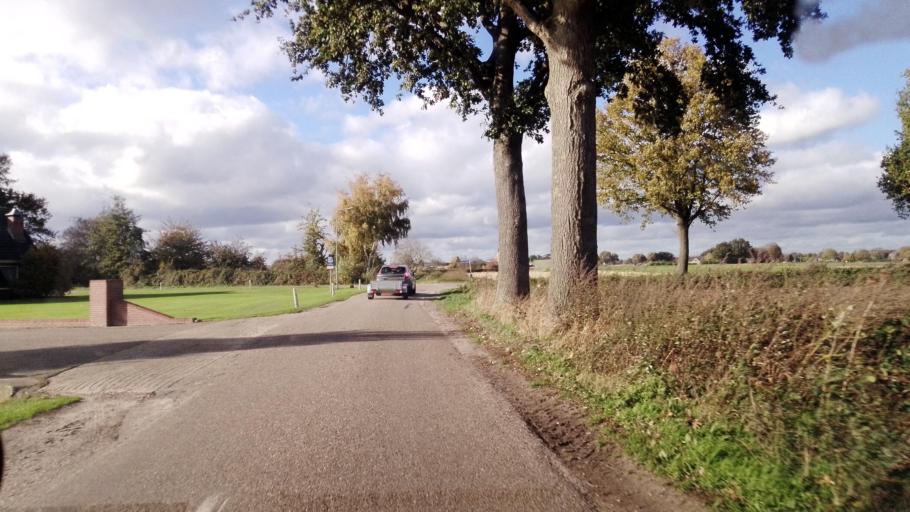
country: NL
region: Limburg
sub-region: Gemeente Venray
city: Venray
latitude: 51.4951
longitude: 5.9673
